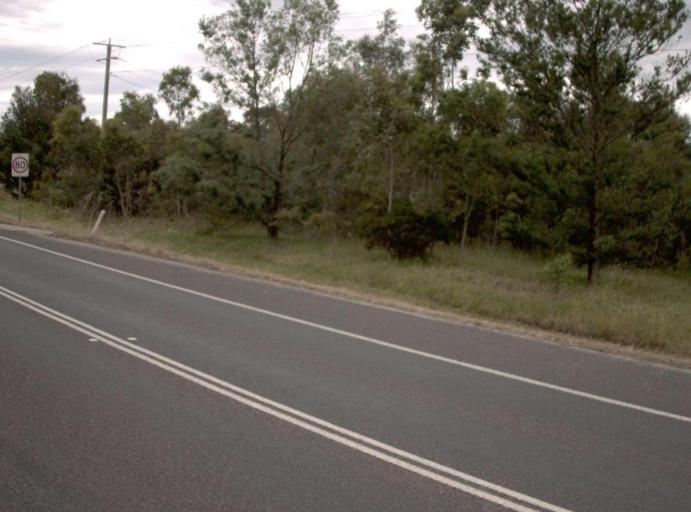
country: AU
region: Victoria
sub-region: Wellington
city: Sale
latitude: -38.1632
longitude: 147.0863
